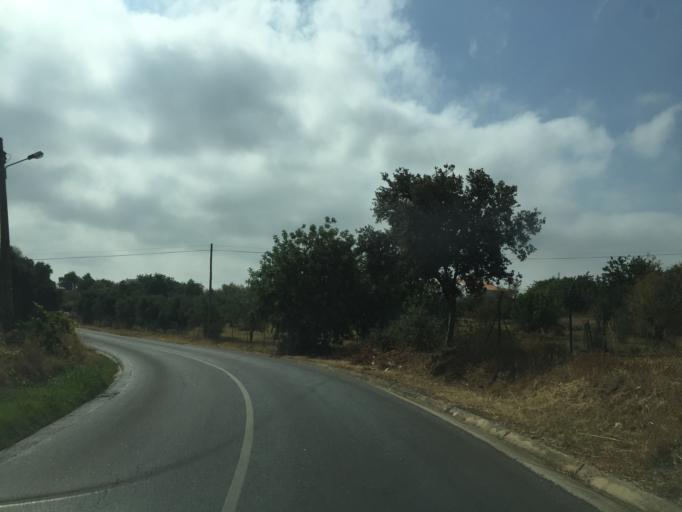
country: PT
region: Faro
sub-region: Olhao
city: Olhao
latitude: 37.0753
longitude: -7.8894
